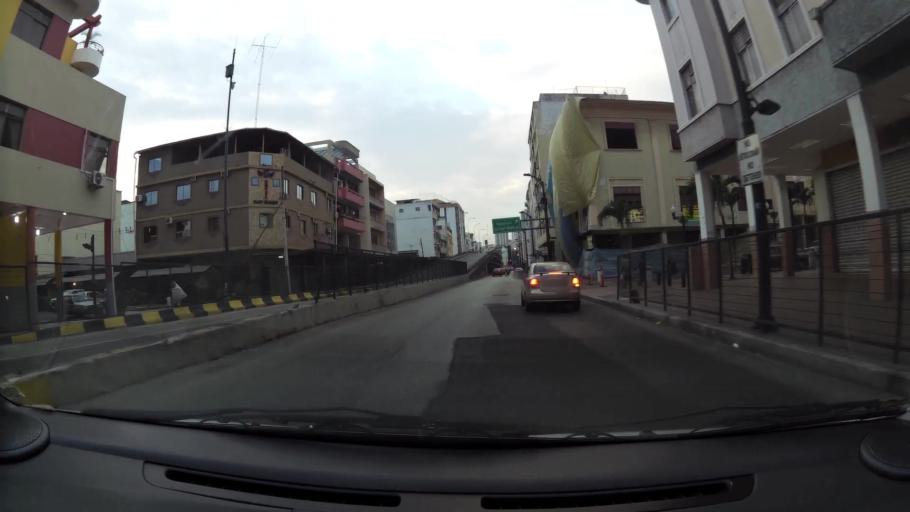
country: EC
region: Guayas
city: Guayaquil
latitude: -2.2024
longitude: -79.8838
